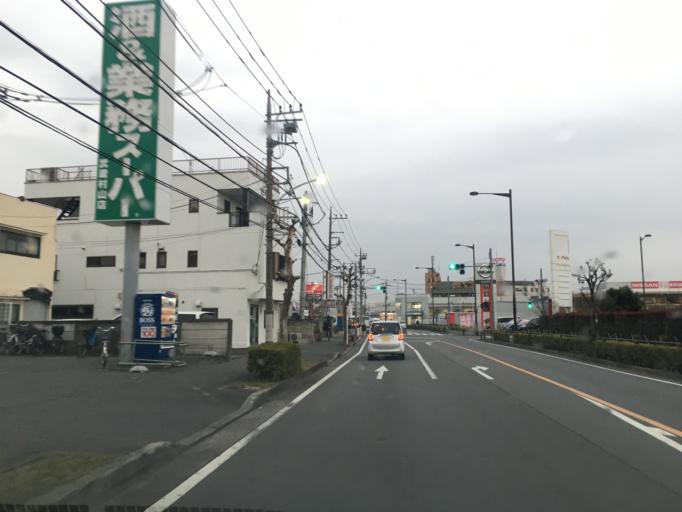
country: JP
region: Tokyo
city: Fussa
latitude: 35.7469
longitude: 139.3890
